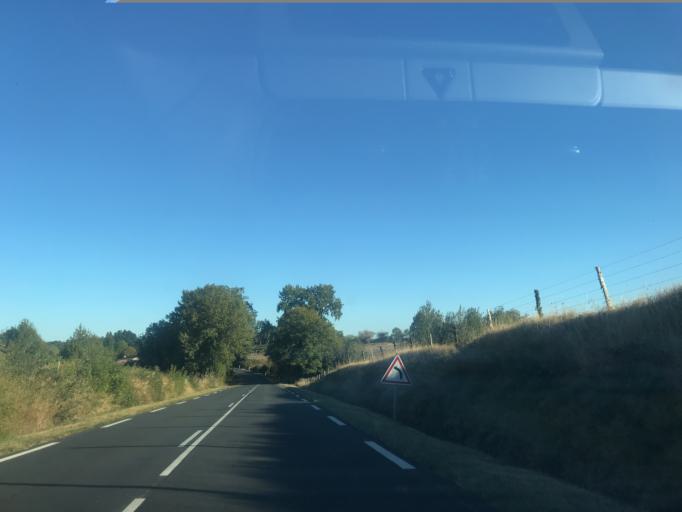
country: FR
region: Poitou-Charentes
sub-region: Departement de la Charente-Maritime
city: Montguyon
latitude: 45.1756
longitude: -0.1132
